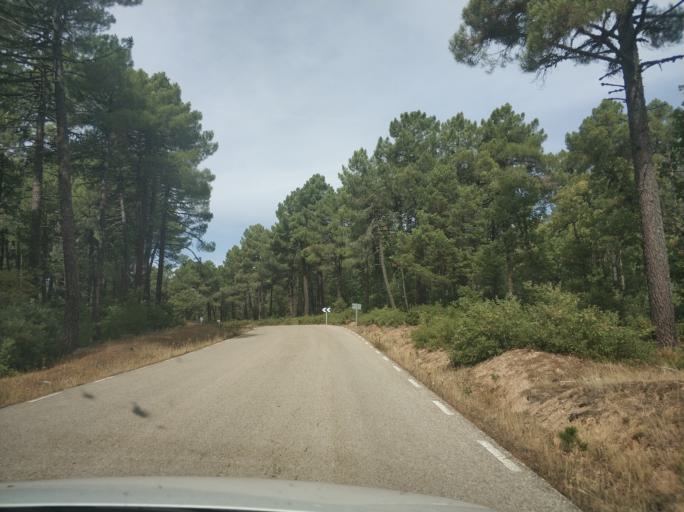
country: ES
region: Castille and Leon
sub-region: Provincia de Soria
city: Duruelo de la Sierra
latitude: 41.8914
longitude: -2.9433
